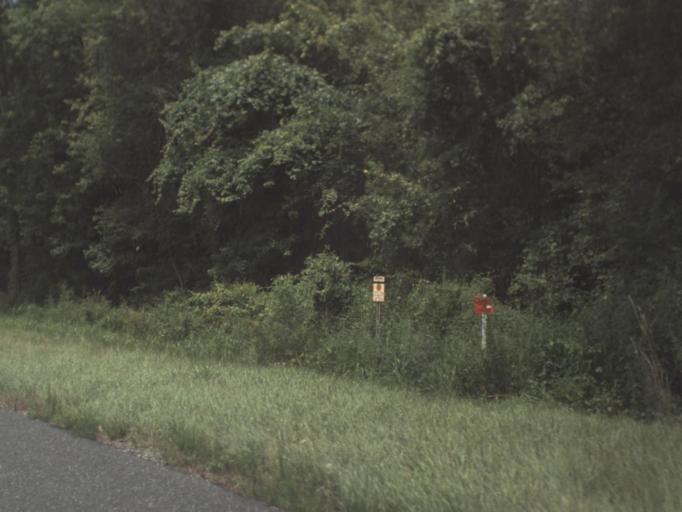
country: US
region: Florida
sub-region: Taylor County
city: Perry
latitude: 30.2215
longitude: -83.6739
